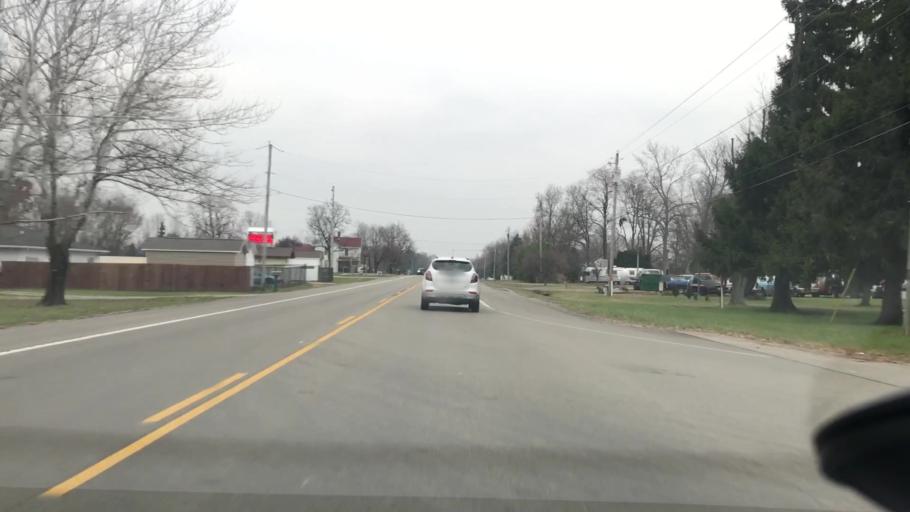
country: US
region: Ohio
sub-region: Greene County
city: Yellow Springs
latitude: 39.8420
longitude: -83.8623
